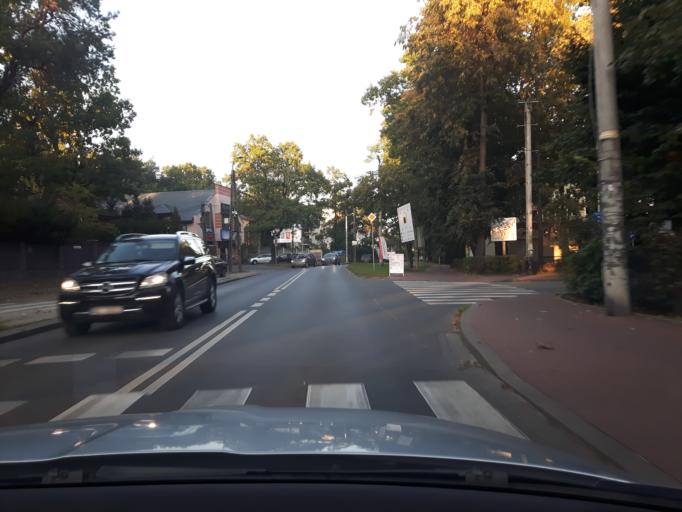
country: PL
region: Masovian Voivodeship
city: Zielonka
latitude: 52.3152
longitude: 21.1582
